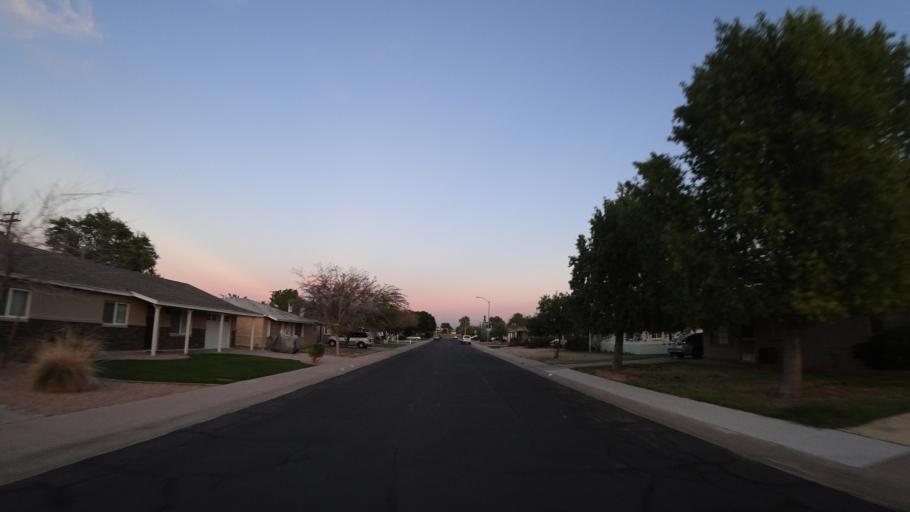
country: US
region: Arizona
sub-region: Maricopa County
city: Scottsdale
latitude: 33.4825
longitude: -111.9155
